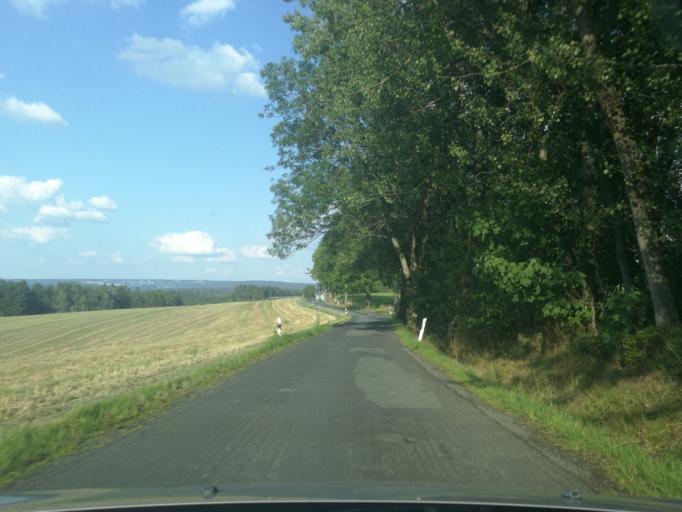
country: DE
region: Saxony
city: Bad Elster
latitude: 50.3127
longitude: 12.2244
